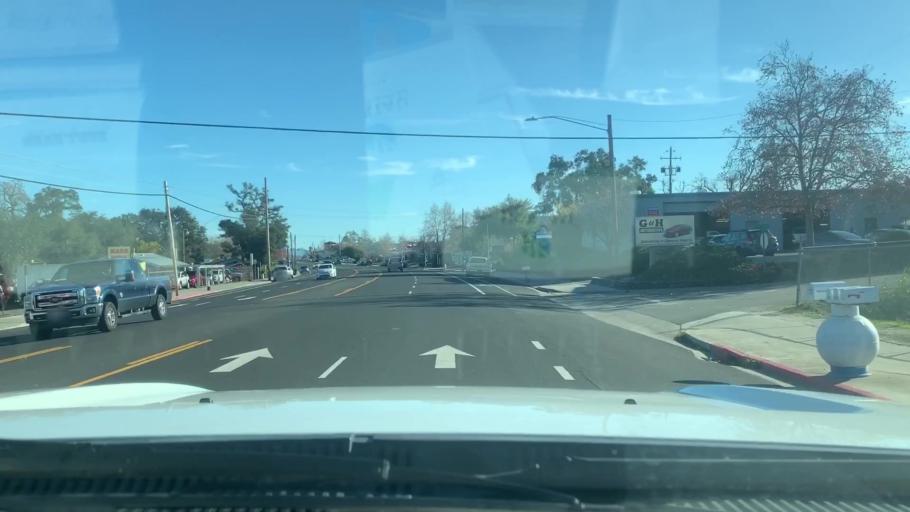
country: US
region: California
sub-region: San Luis Obispo County
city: Atascadero
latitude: 35.4702
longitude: -120.6527
